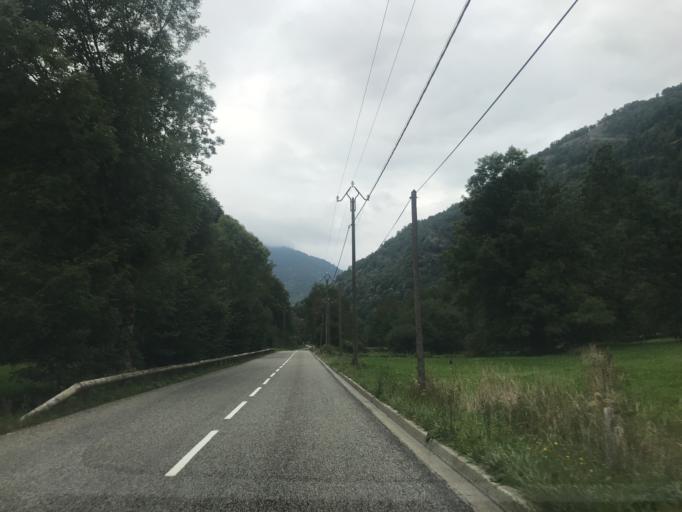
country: FR
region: Midi-Pyrenees
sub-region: Departement de la Haute-Garonne
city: Bagneres-de-Luchon
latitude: 42.7696
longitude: 0.6315
